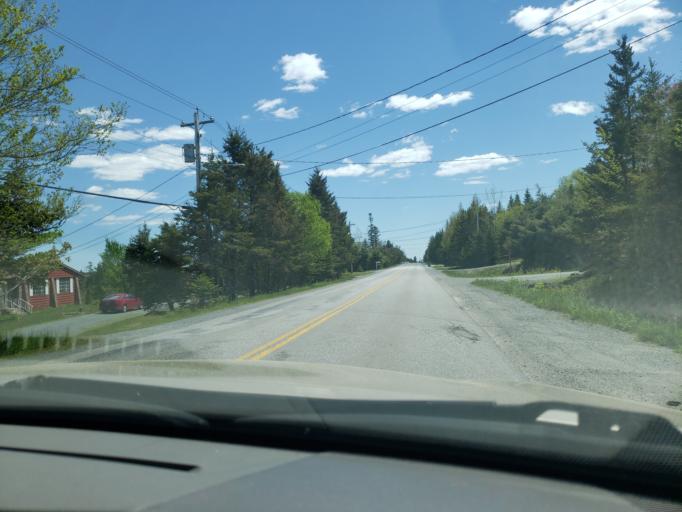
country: CA
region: Nova Scotia
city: Cole Harbour
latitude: 44.7349
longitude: -63.3097
